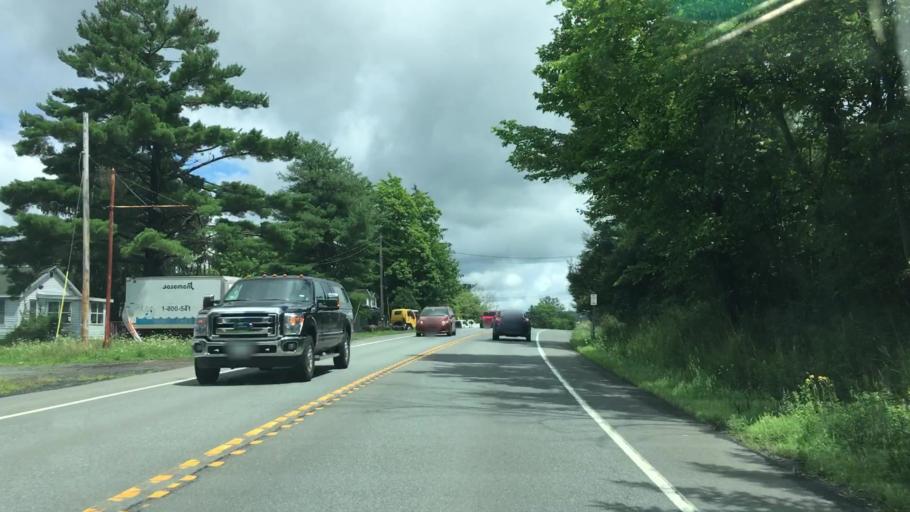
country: US
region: New York
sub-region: Rensselaer County
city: Hoosick Falls
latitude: 42.8467
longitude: -73.4470
